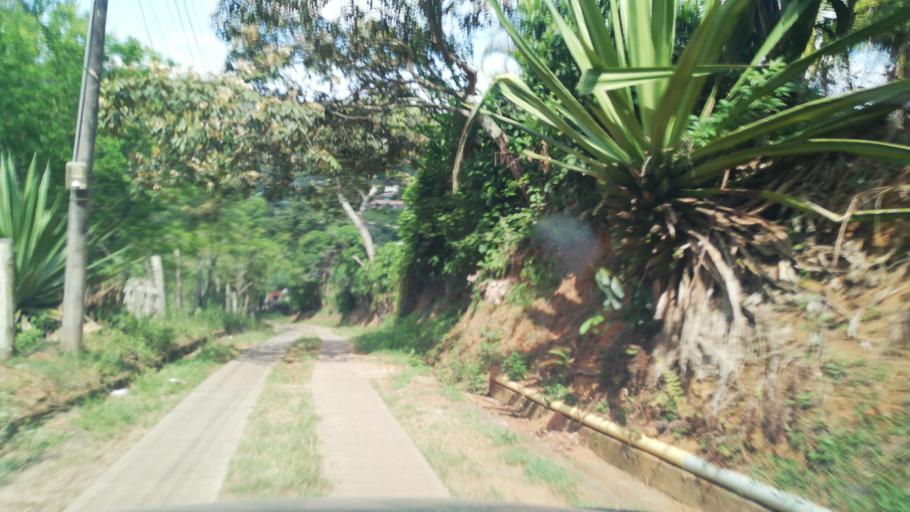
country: CO
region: Valle del Cauca
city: Cali
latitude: 3.4820
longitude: -76.5551
